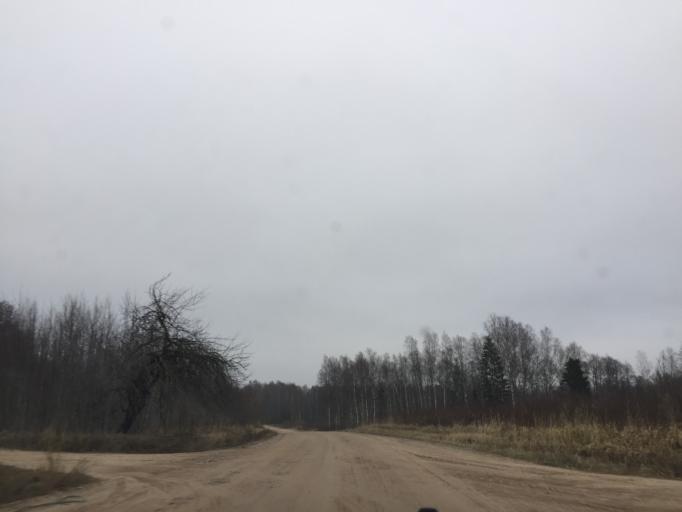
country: LV
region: Limbazu Rajons
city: Limbazi
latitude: 57.6038
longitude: 24.5622
